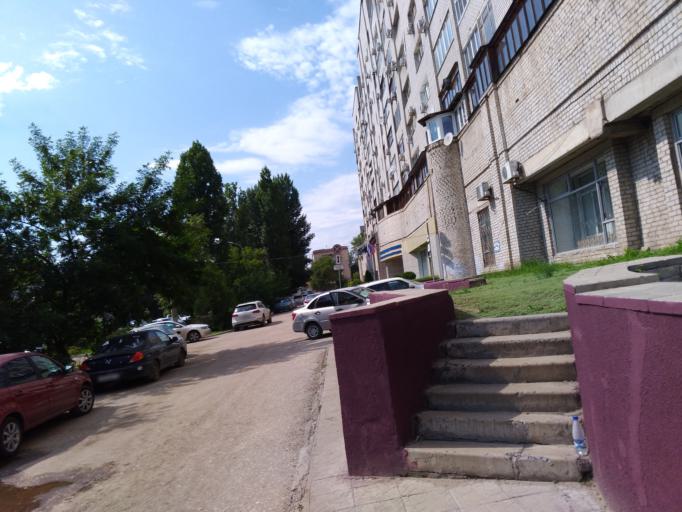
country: RU
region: Volgograd
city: Volgograd
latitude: 48.7124
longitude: 44.5013
